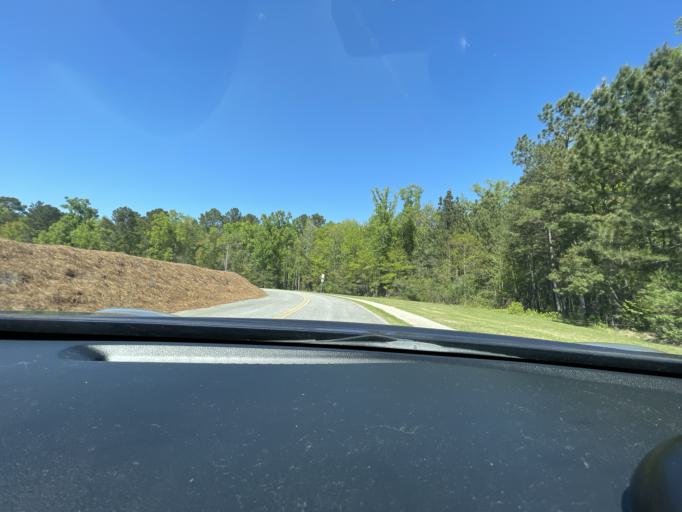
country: US
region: Georgia
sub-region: Chatham County
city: Pooler
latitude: 32.1300
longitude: -81.2611
